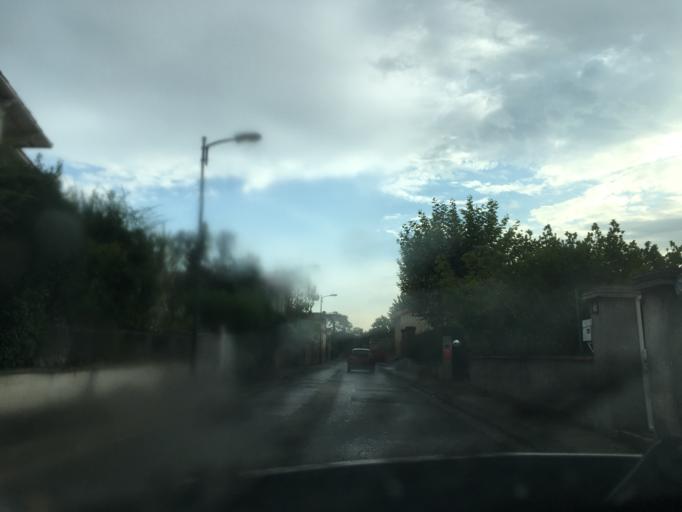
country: FR
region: Midi-Pyrenees
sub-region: Departement de la Haute-Garonne
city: Cugnaux
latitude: 43.5577
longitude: 1.3808
